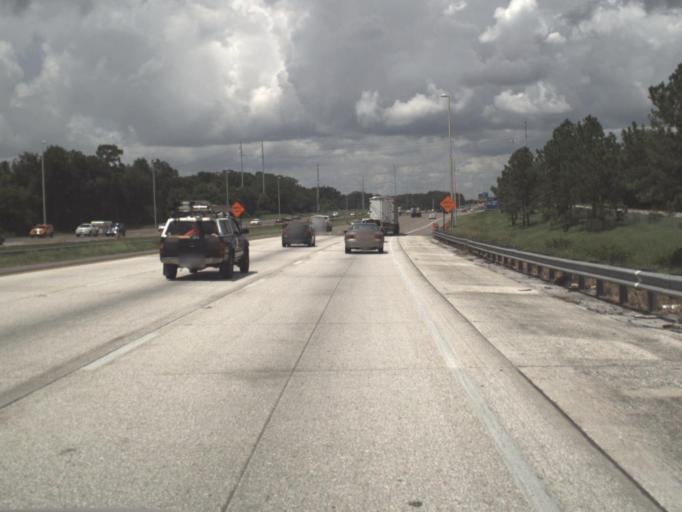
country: US
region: Florida
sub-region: Hillsborough County
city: Temple Terrace
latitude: 28.0404
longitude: -82.3504
